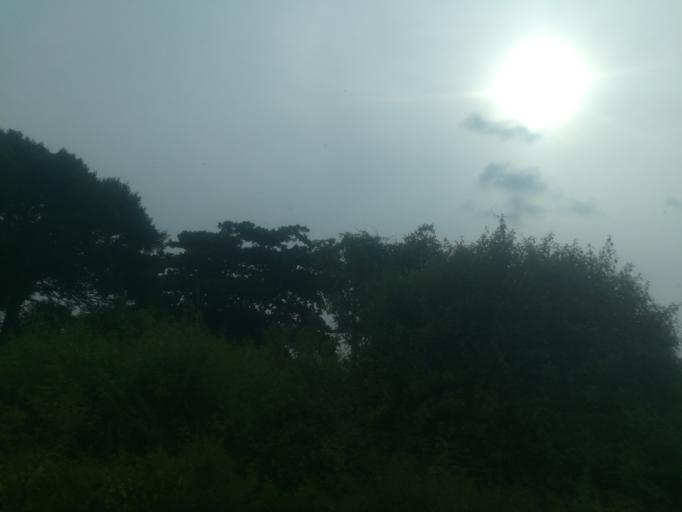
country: NG
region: Ogun
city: Ayetoro
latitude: 7.2863
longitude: 3.0856
